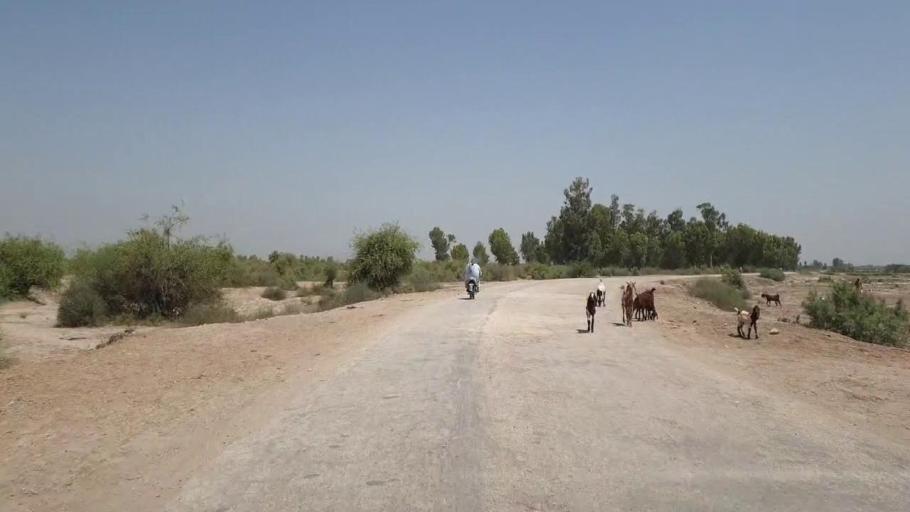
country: PK
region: Sindh
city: Adilpur
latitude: 27.8946
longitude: 69.2892
